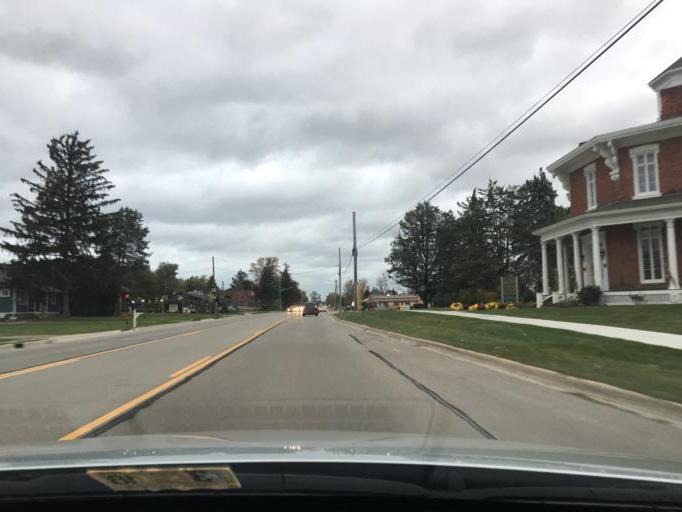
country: US
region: Michigan
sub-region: Macomb County
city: Shelby
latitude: 42.7170
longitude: -83.0355
